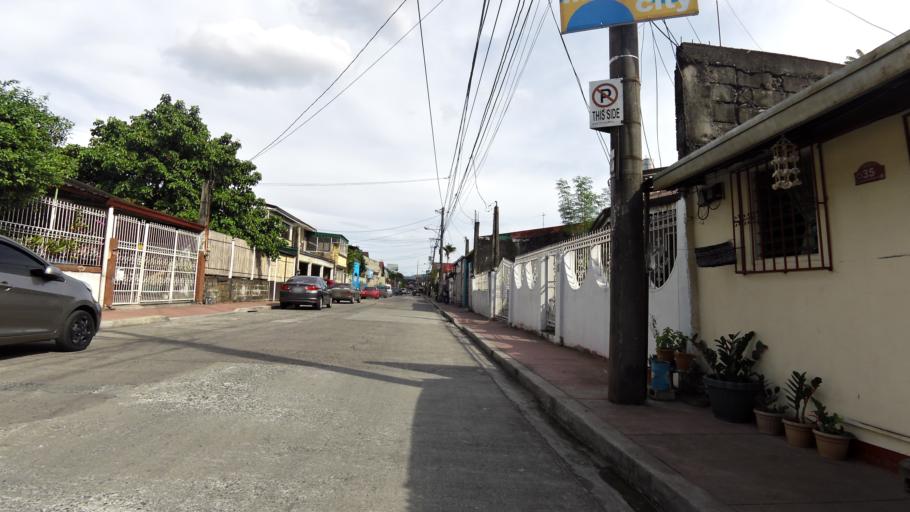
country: PH
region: Metro Manila
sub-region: Marikina
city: Calumpang
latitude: 14.6216
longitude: 121.0988
